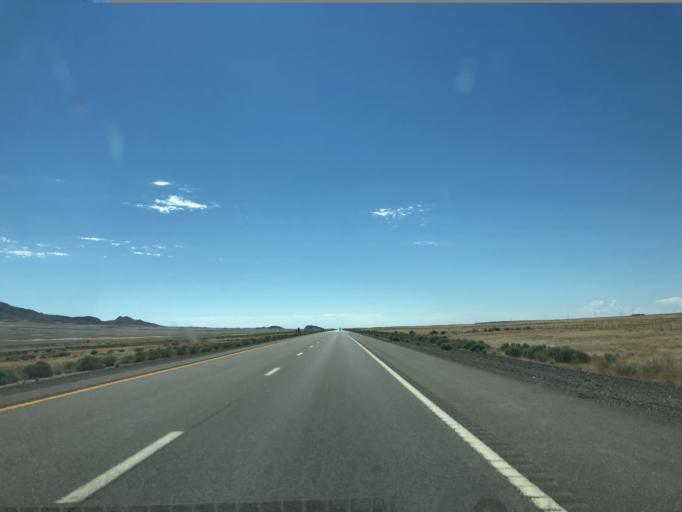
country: US
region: Nevada
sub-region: Elko County
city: West Wendover
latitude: 40.8131
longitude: -114.1807
